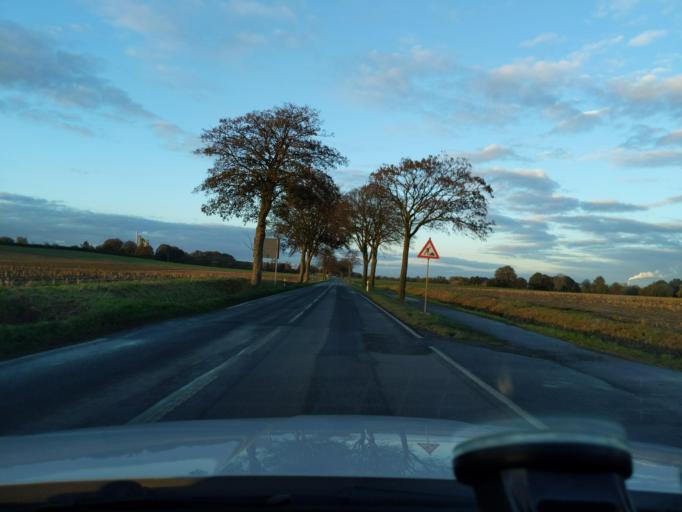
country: DE
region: North Rhine-Westphalia
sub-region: Regierungsbezirk Dusseldorf
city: Uedem
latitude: 51.6871
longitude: 6.3196
